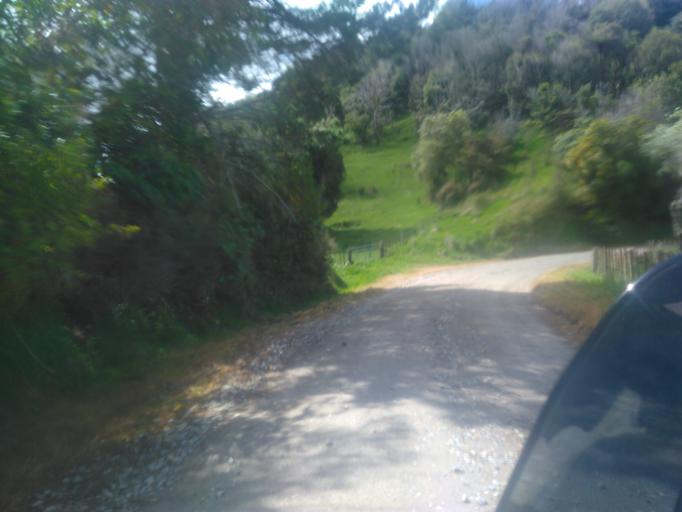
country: NZ
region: Hawke's Bay
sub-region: Wairoa District
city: Wairoa
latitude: -38.7775
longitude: 177.6223
